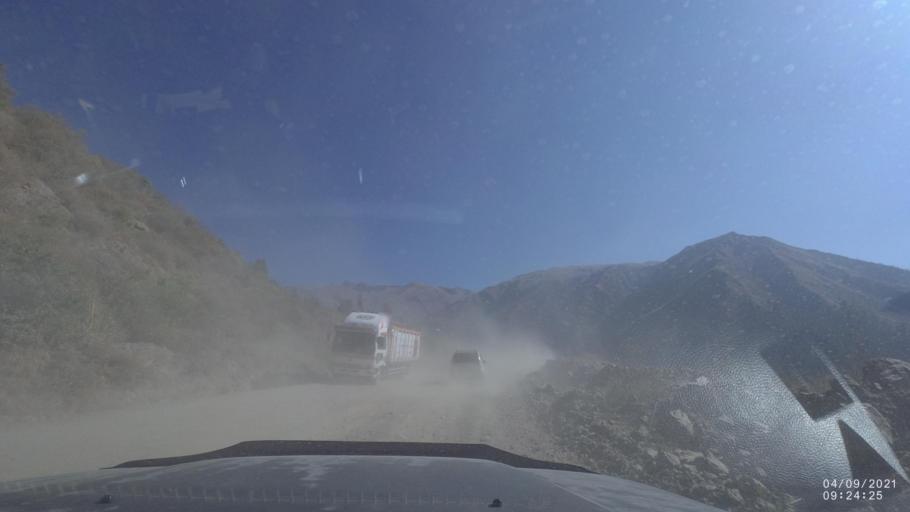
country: BO
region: Cochabamba
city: Sipe Sipe
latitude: -17.3596
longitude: -66.3682
